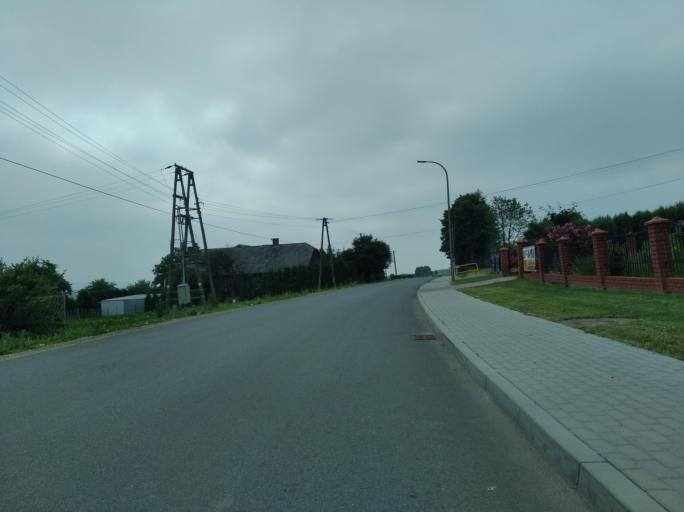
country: PL
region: Subcarpathian Voivodeship
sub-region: Powiat krosnienski
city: Sieniawa
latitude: 49.6016
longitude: 21.9045
